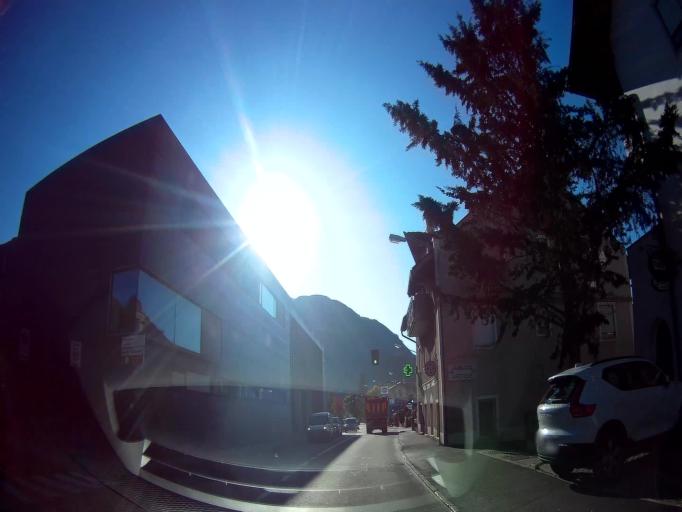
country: IT
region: Trentino-Alto Adige
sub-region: Bolzano
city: Merano
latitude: 46.6574
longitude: 11.1673
